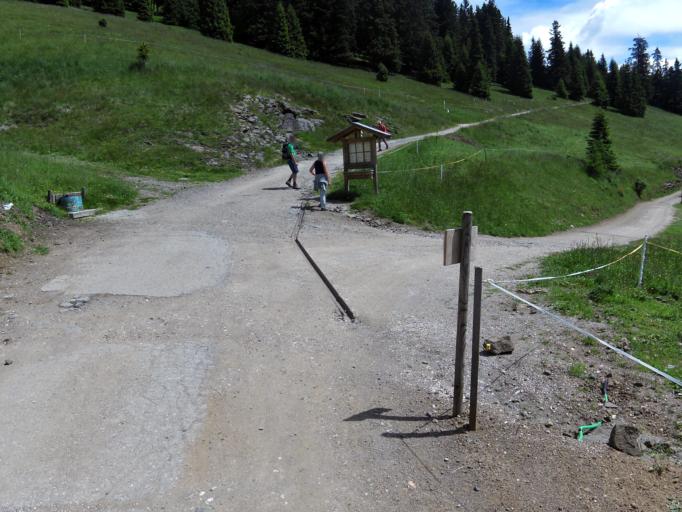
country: IT
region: Trentino-Alto Adige
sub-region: Bolzano
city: Ortisei
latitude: 46.5550
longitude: 11.6609
